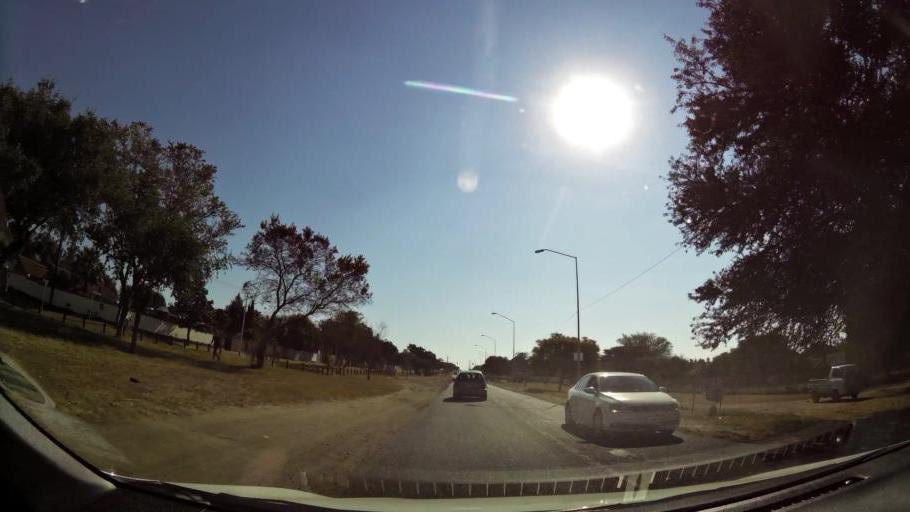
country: ZA
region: Gauteng
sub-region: City of Tshwane Metropolitan Municipality
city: Pretoria
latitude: -25.8010
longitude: 28.2916
